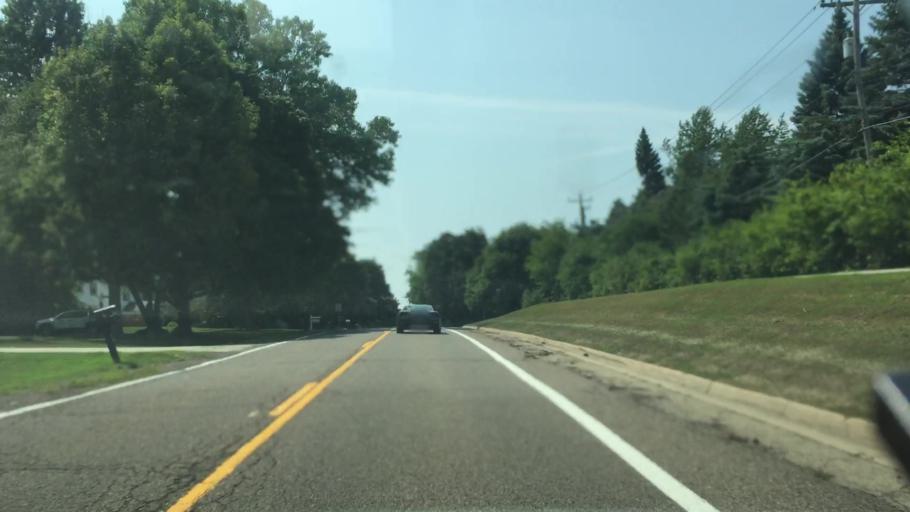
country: US
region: Michigan
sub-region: Oakland County
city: Franklin
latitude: 42.5583
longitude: -83.3138
